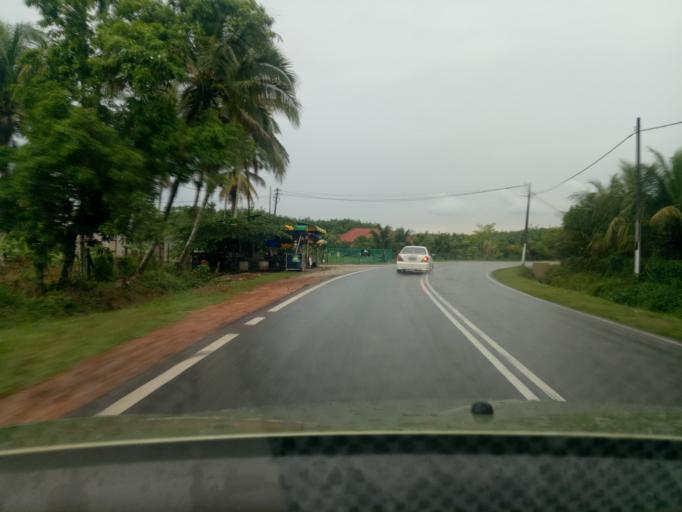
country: MY
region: Penang
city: Tasek Glugor
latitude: 5.5491
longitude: 100.5733
